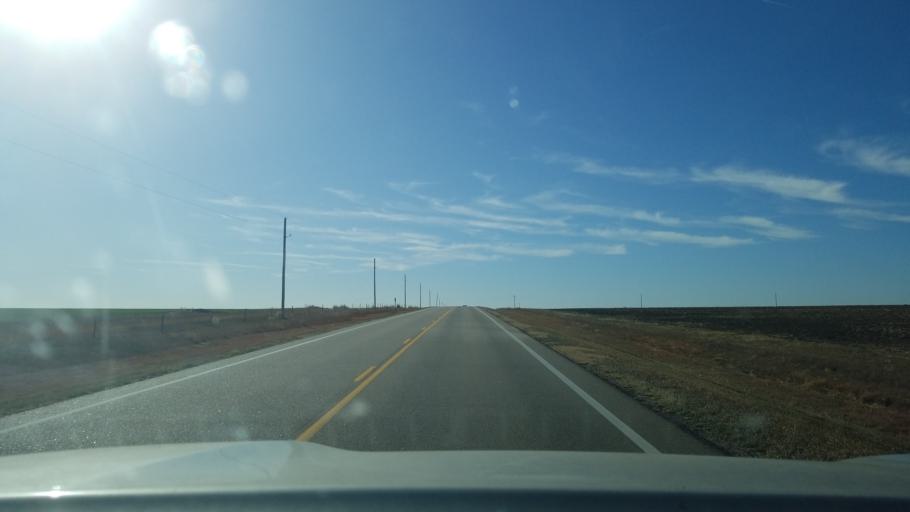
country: US
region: Kansas
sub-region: Ness County
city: Ness City
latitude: 38.3965
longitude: -99.8984
